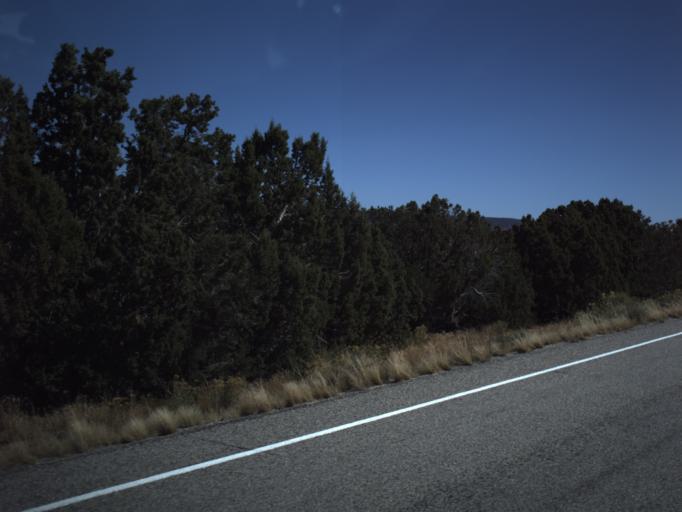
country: US
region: Utah
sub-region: San Juan County
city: Blanding
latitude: 37.5408
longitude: -109.9697
